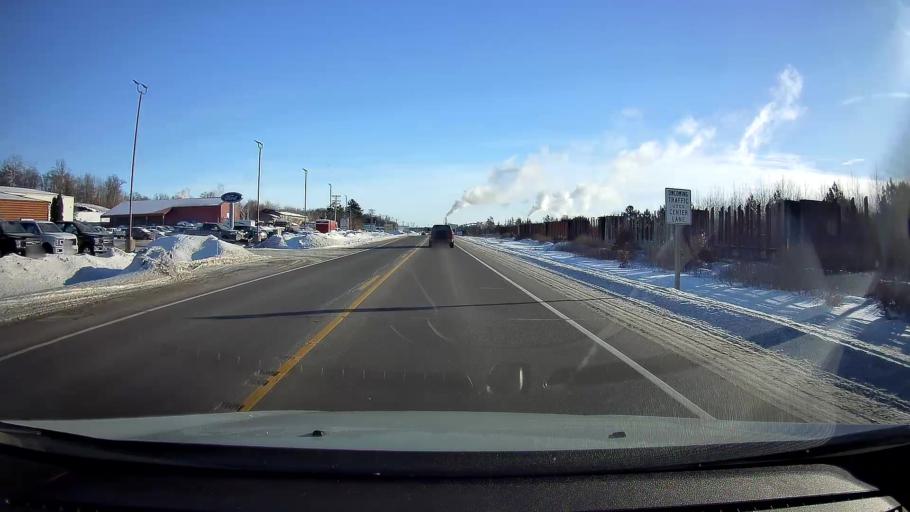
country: US
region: Wisconsin
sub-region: Sawyer County
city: Hayward
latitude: 45.9848
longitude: -91.5368
